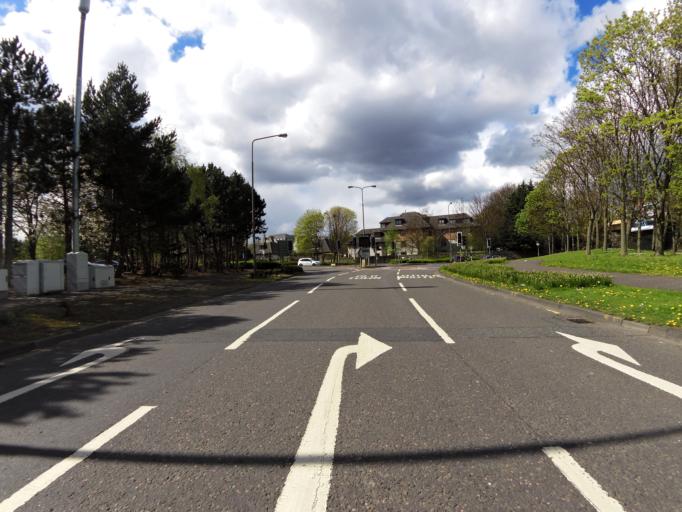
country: GB
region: Scotland
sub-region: West Lothian
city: Seafield
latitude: 55.9285
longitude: -3.1618
